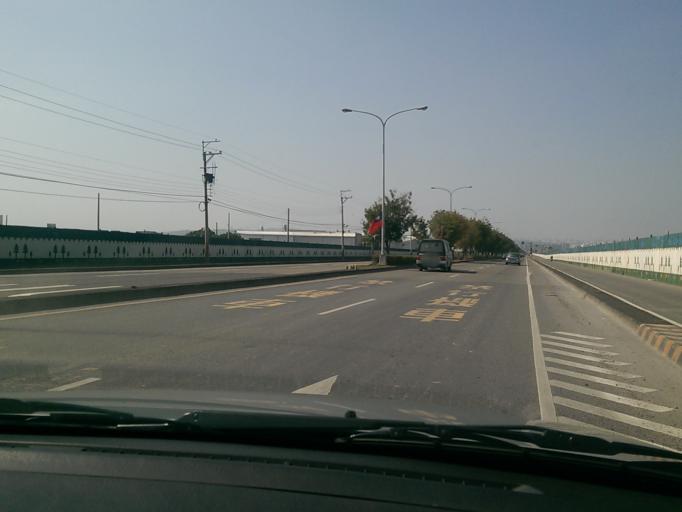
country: TW
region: Taiwan
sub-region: Taichung City
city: Taichung
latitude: 24.1188
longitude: 120.6386
